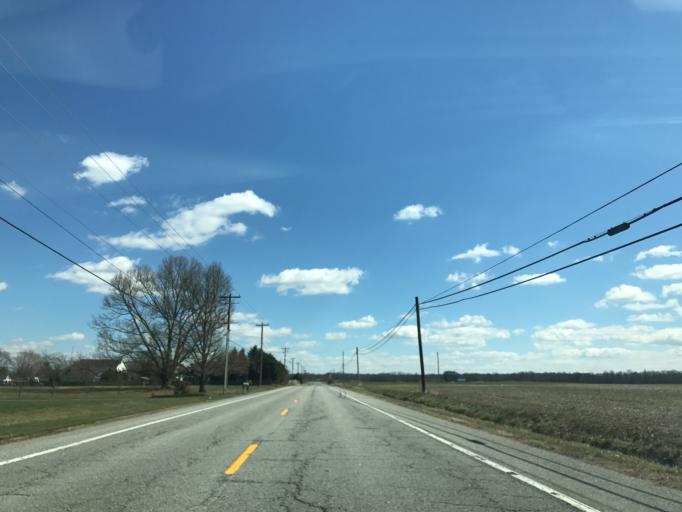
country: US
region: Maryland
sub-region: Queen Anne's County
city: Centreville
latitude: 39.0310
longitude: -76.0427
